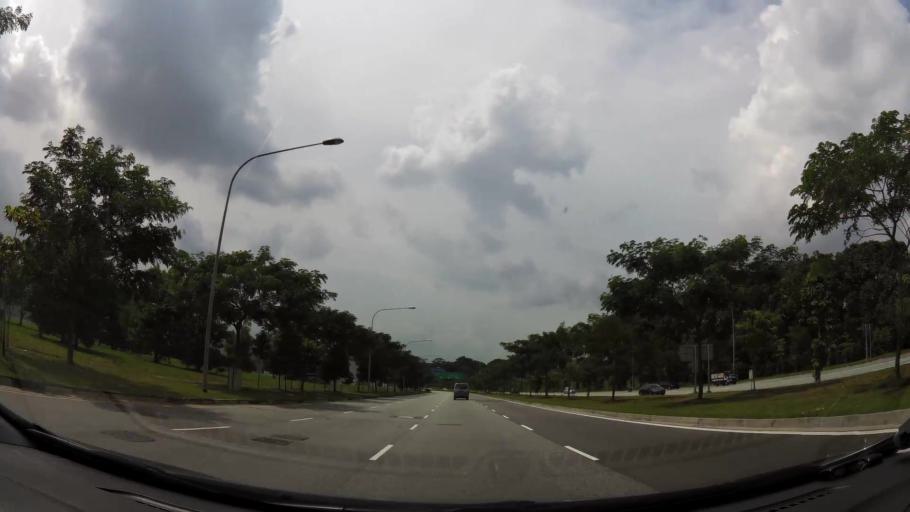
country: MY
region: Johor
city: Kampung Pasir Gudang Baru
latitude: 1.4068
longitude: 103.8571
